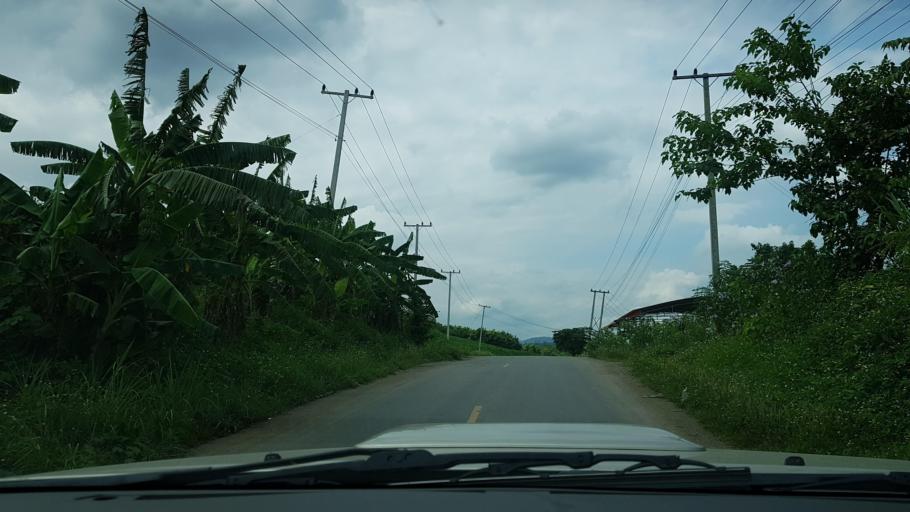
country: LA
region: Loungnamtha
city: Muang Nale
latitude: 20.0414
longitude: 101.3486
